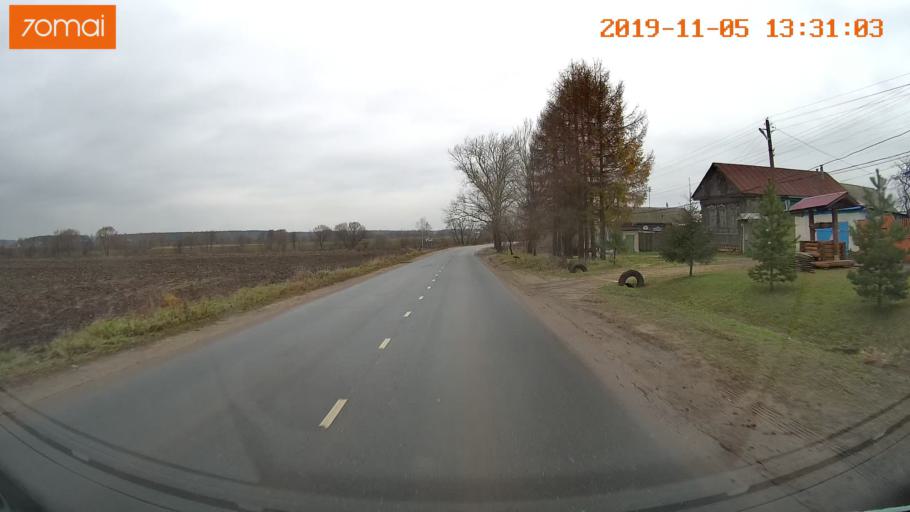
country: RU
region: Ivanovo
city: Shuya
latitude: 56.8718
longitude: 41.3928
